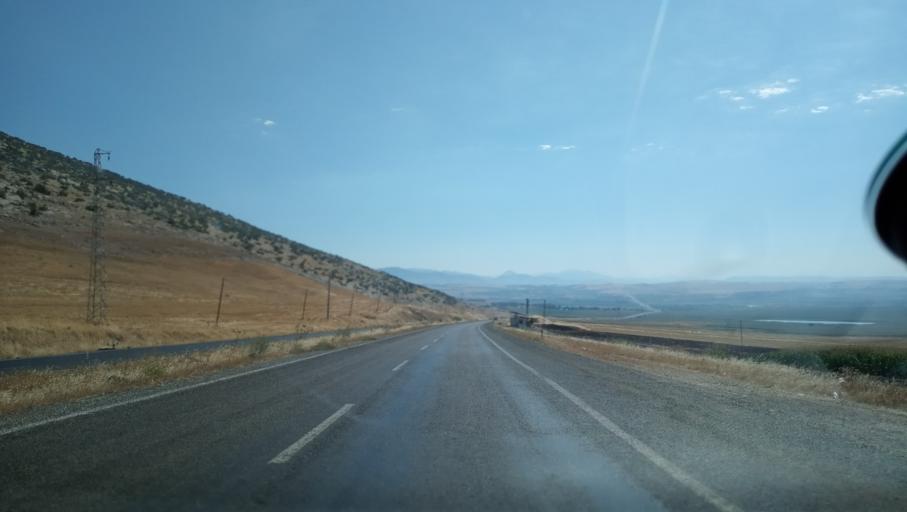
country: TR
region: Diyarbakir
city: Malabadi
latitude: 38.1251
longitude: 41.1616
